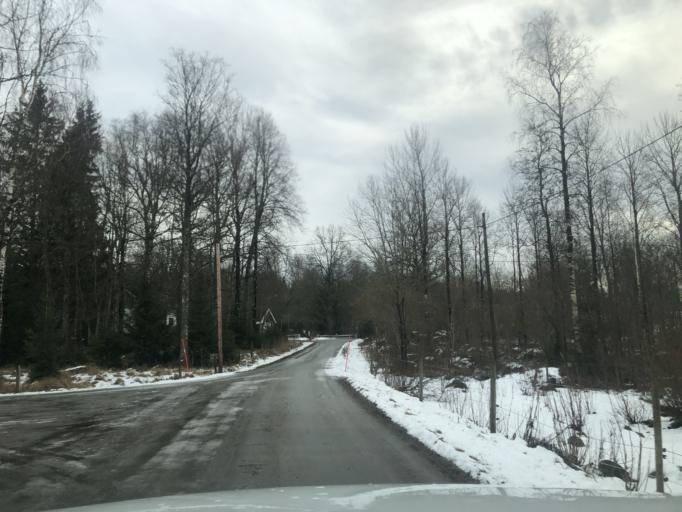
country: SE
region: Vaestra Goetaland
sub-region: Ulricehamns Kommun
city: Ulricehamn
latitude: 57.7703
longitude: 13.4697
